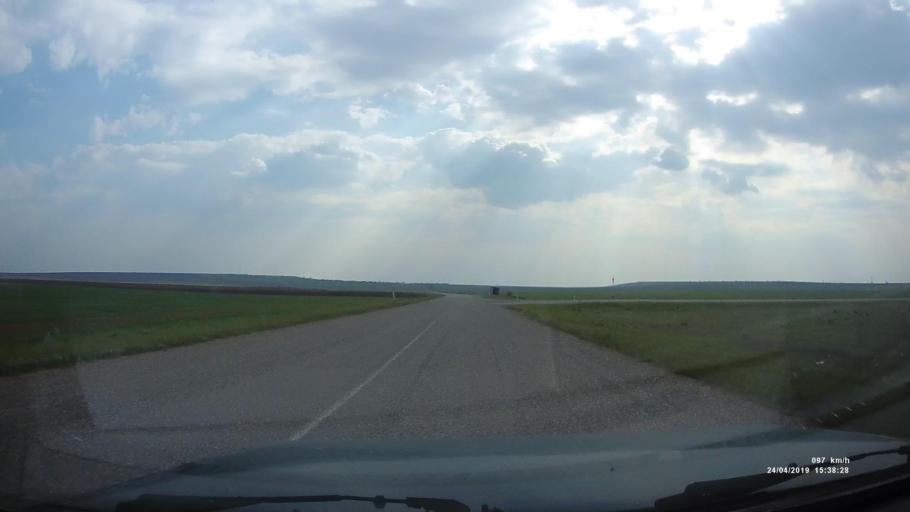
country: RU
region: Kalmykiya
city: Yashalta
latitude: 46.5976
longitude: 42.8273
